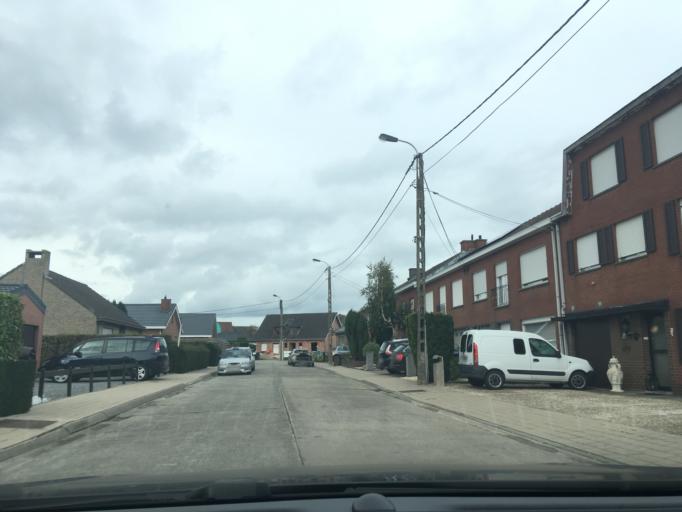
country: BE
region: Flanders
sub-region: Provincie West-Vlaanderen
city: Moorslede
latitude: 50.8960
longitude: 3.0632
